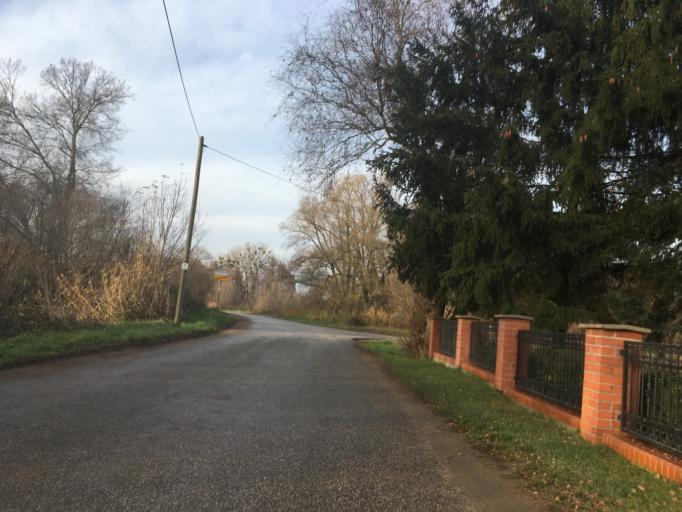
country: DE
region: Brandenburg
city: Bad Freienwalde
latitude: 52.7959
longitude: 14.0307
